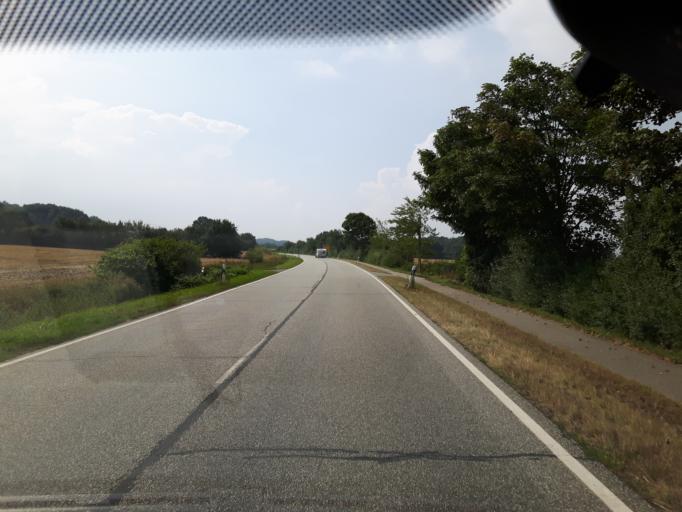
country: DE
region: Schleswig-Holstein
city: Goosefeld
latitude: 54.4216
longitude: 9.8028
